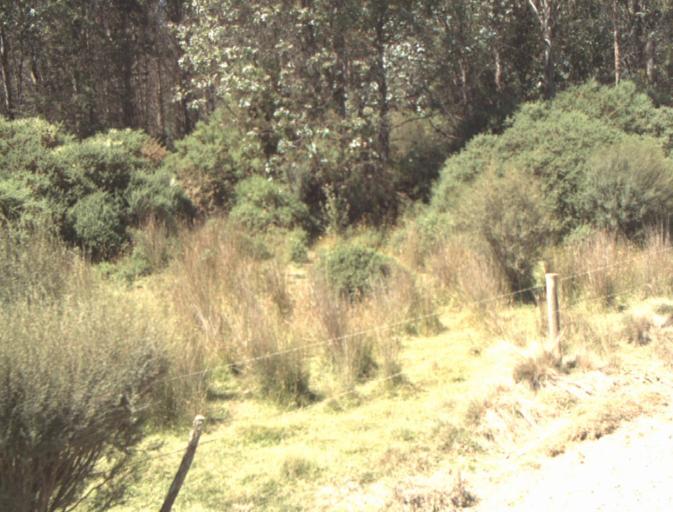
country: AU
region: Tasmania
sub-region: Dorset
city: Scottsdale
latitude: -41.3235
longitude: 147.4728
